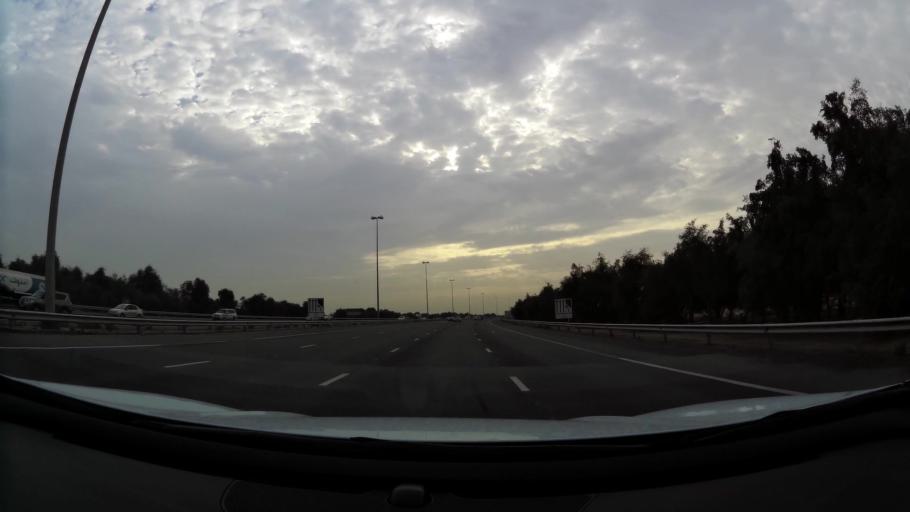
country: AE
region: Abu Dhabi
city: Abu Dhabi
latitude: 24.3036
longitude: 54.6161
